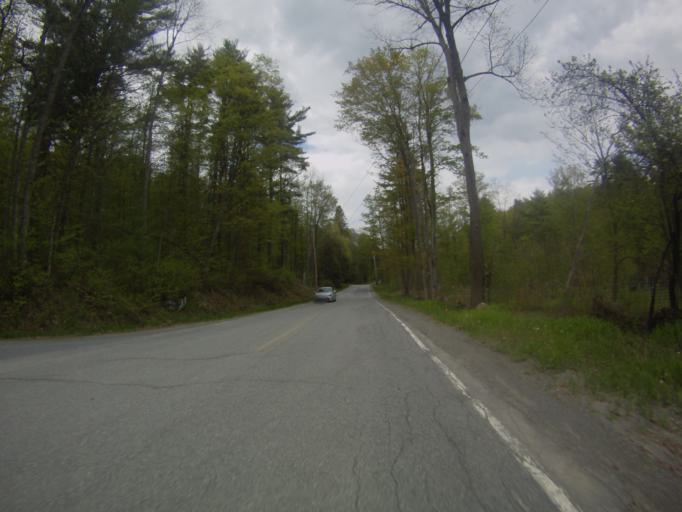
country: US
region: New York
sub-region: Essex County
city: Port Henry
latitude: 43.9401
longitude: -73.5036
